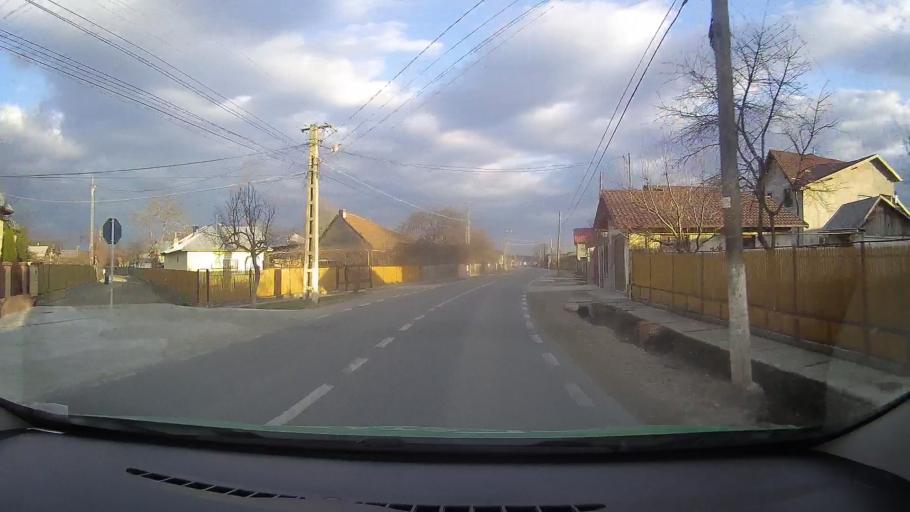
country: RO
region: Dambovita
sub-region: Comuna I. L. Caragiale
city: Ghirdoveni
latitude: 44.9455
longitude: 25.6630
